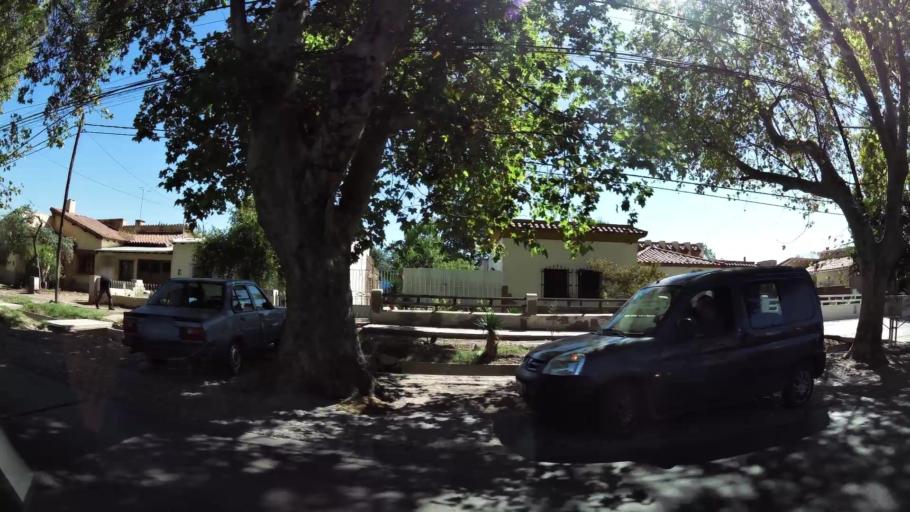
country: AR
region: Mendoza
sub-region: Departamento de Godoy Cruz
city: Godoy Cruz
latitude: -32.9444
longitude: -68.8135
